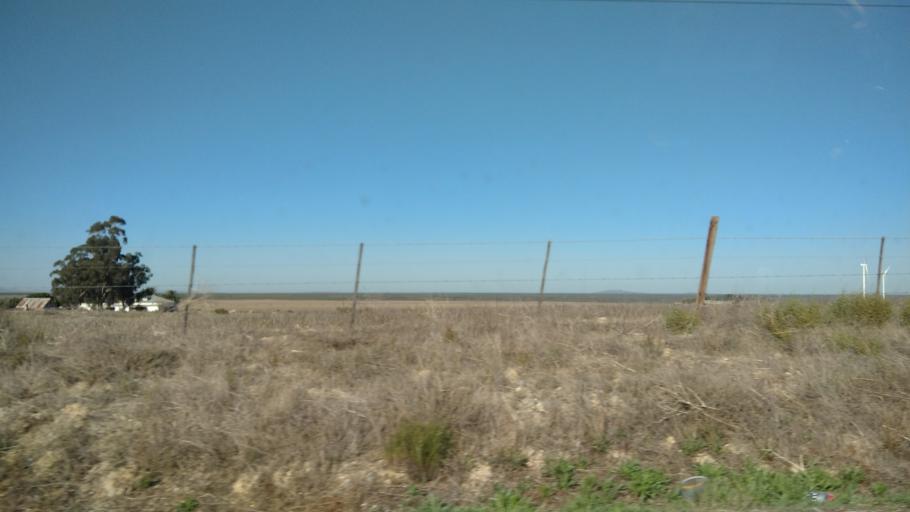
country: ZA
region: Western Cape
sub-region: West Coast District Municipality
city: Moorreesburg
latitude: -33.0956
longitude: 18.4153
